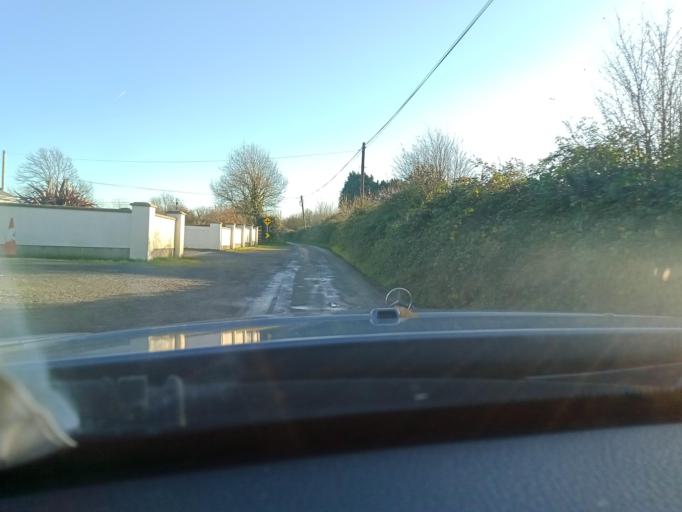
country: IE
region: Leinster
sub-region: Kilkenny
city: Mooncoin
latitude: 52.2943
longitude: -7.1828
